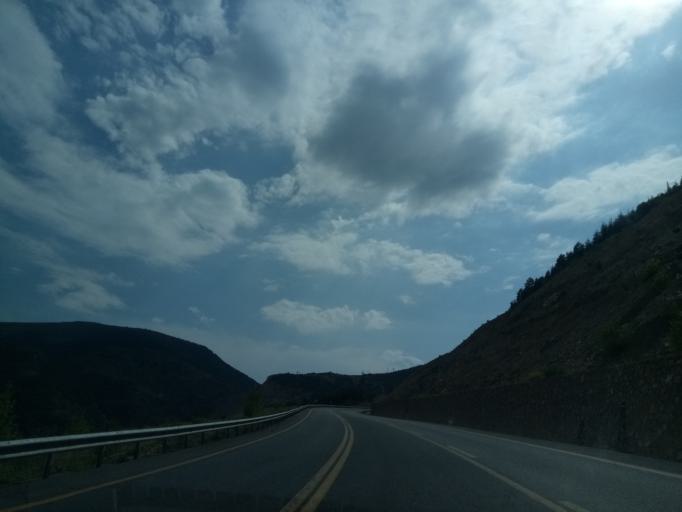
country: TR
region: Konya
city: Aksehir
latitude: 38.3004
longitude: 31.4539
